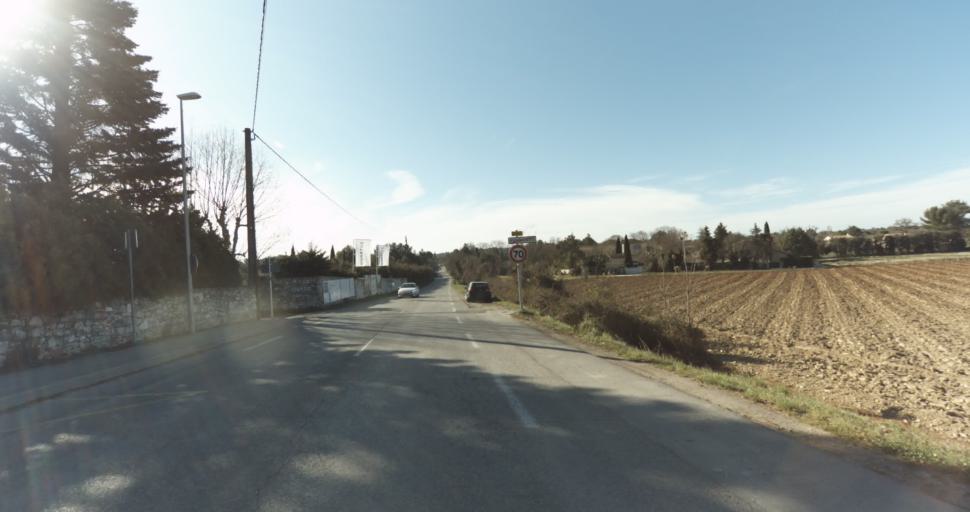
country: FR
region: Provence-Alpes-Cote d'Azur
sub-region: Departement des Bouches-du-Rhone
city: Aix-en-Provence
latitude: 43.5733
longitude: 5.4232
